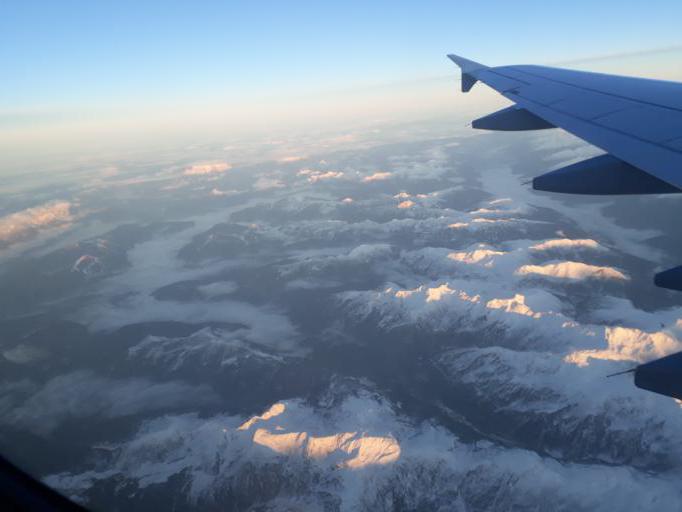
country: AT
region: Tyrol
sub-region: Politischer Bezirk Schwaz
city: Stummerberg
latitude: 47.3054
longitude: 11.9145
